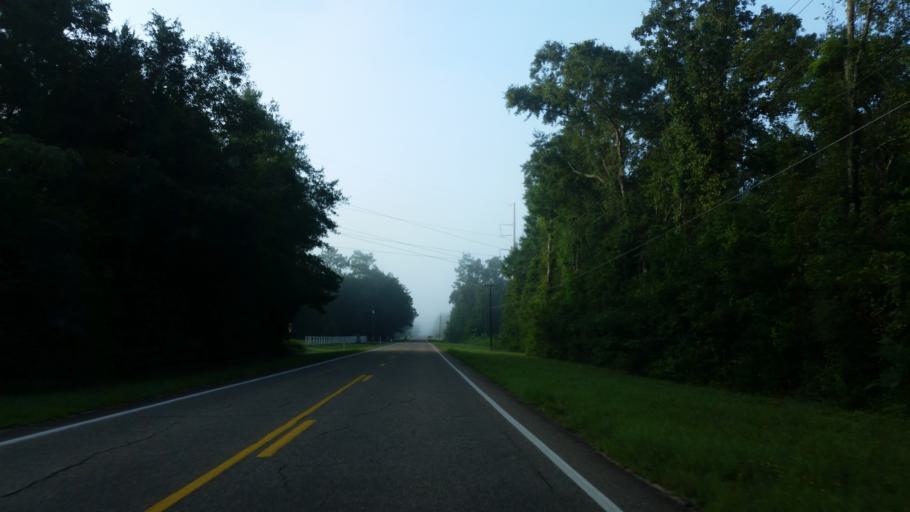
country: US
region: Florida
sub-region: Escambia County
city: Molino
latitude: 30.7379
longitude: -87.3477
